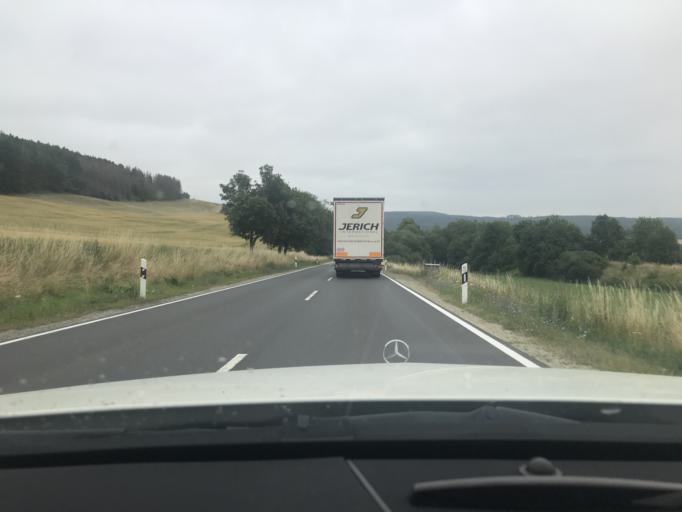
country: DE
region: Thuringia
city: Worbis
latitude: 51.4083
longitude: 10.3481
